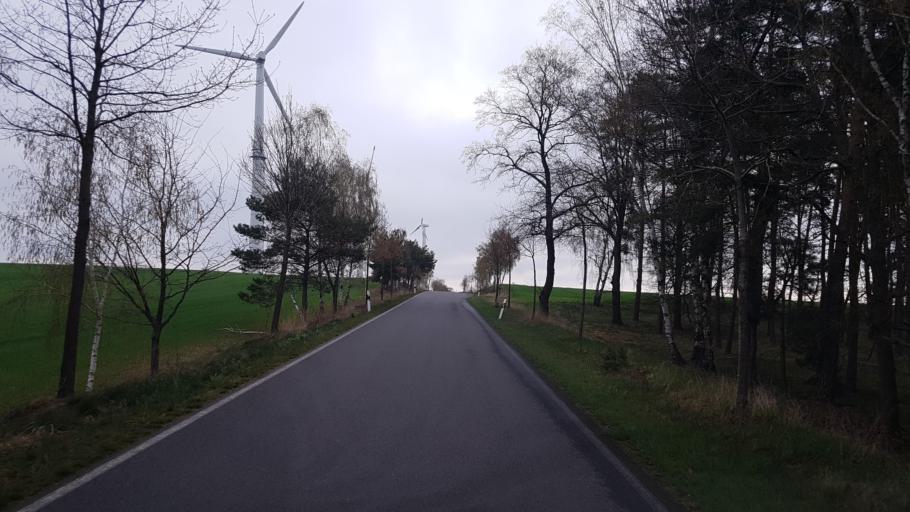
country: DE
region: Brandenburg
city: Drahnsdorf
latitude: 51.9078
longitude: 13.5602
